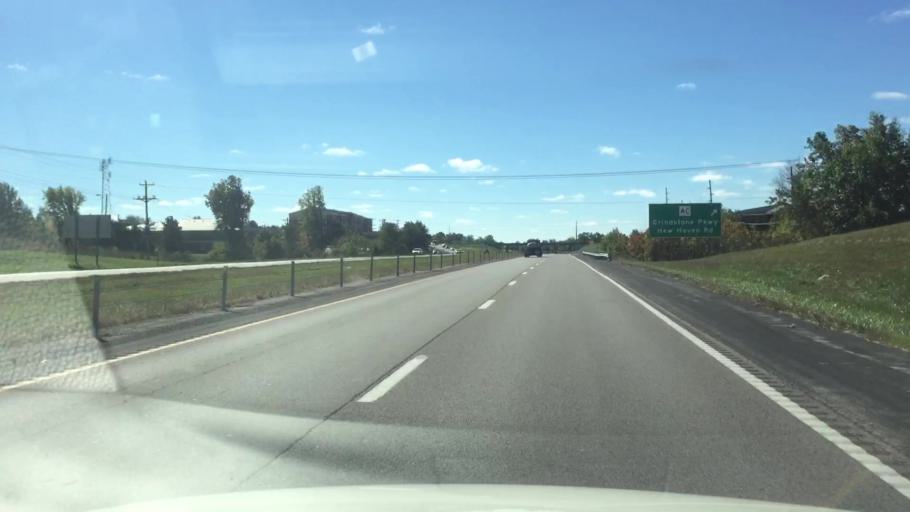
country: US
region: Missouri
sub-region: Boone County
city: Columbia
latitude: 38.9185
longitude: -92.2942
